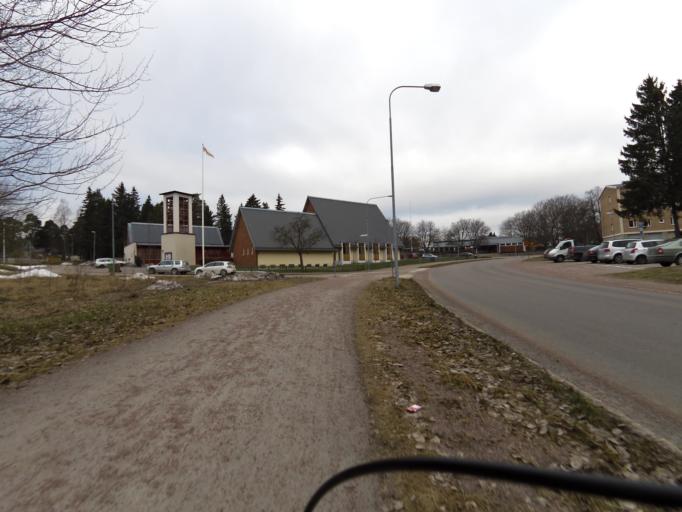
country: SE
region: Gaevleborg
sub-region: Gavle Kommun
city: Gavle
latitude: 60.6593
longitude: 17.1466
